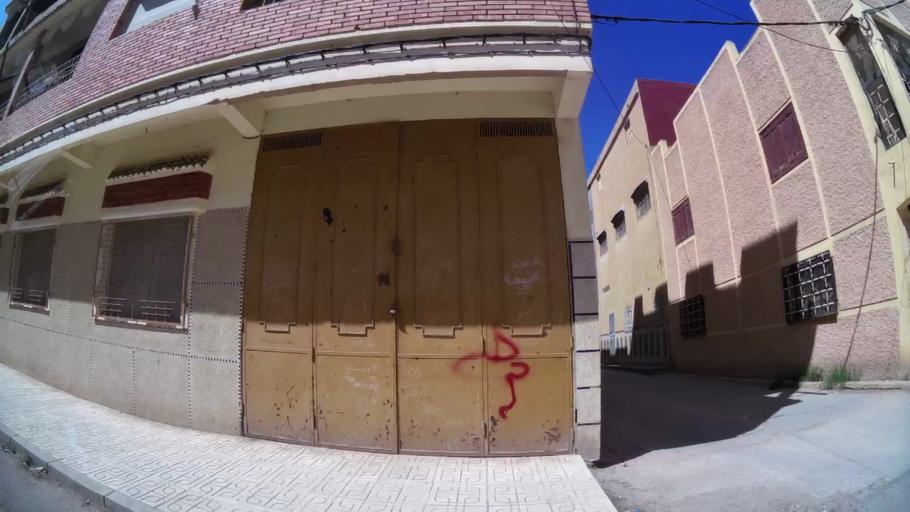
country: MA
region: Oriental
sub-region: Oujda-Angad
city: Oujda
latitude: 34.6715
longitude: -1.9417
